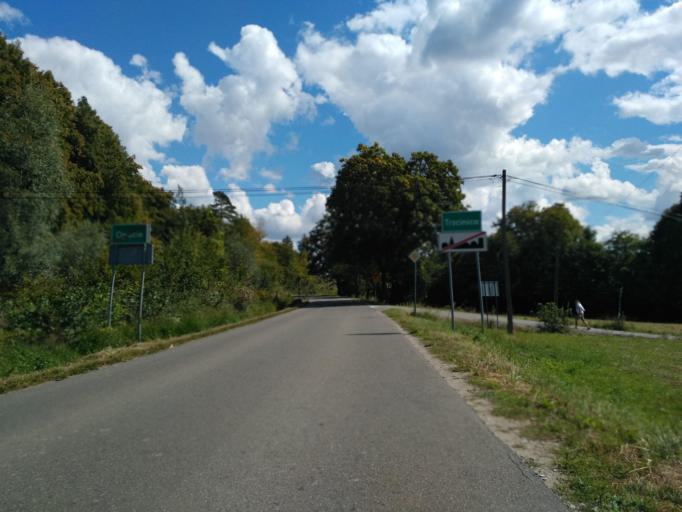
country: PL
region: Subcarpathian Voivodeship
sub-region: Powiat jasielski
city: Trzcinica
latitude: 49.7569
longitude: 21.4055
